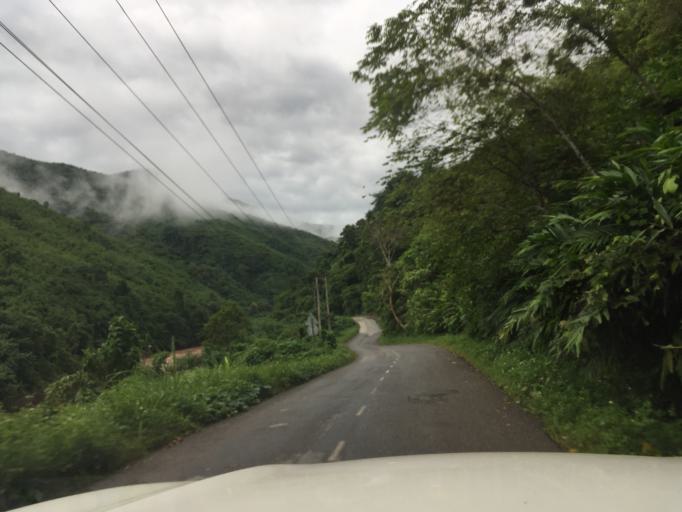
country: LA
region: Oudomxai
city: Muang La
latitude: 21.0457
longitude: 102.2410
